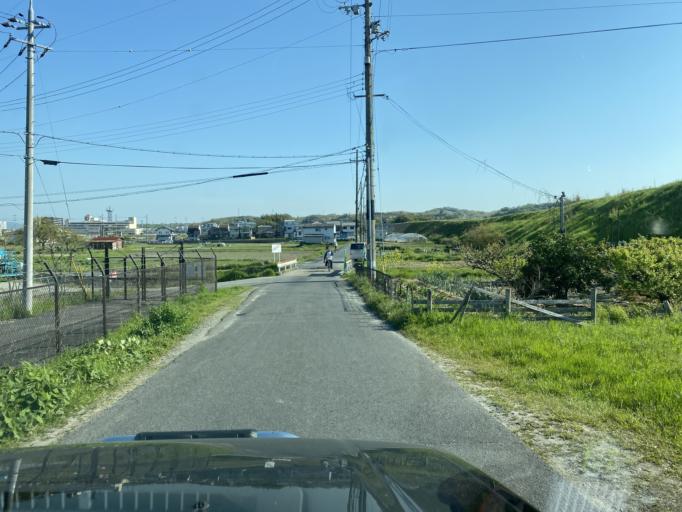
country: JP
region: Kyoto
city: Tanabe
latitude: 34.8300
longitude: 135.7652
